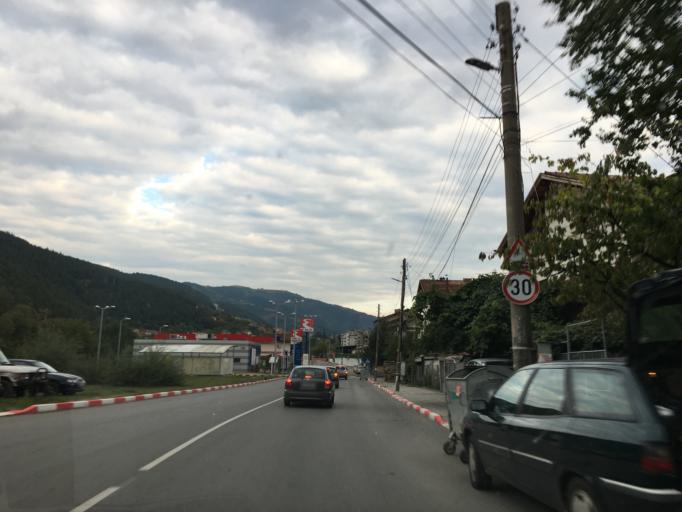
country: BG
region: Sofiya
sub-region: Obshtina Svoge
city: Svoge
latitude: 42.9619
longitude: 23.3466
